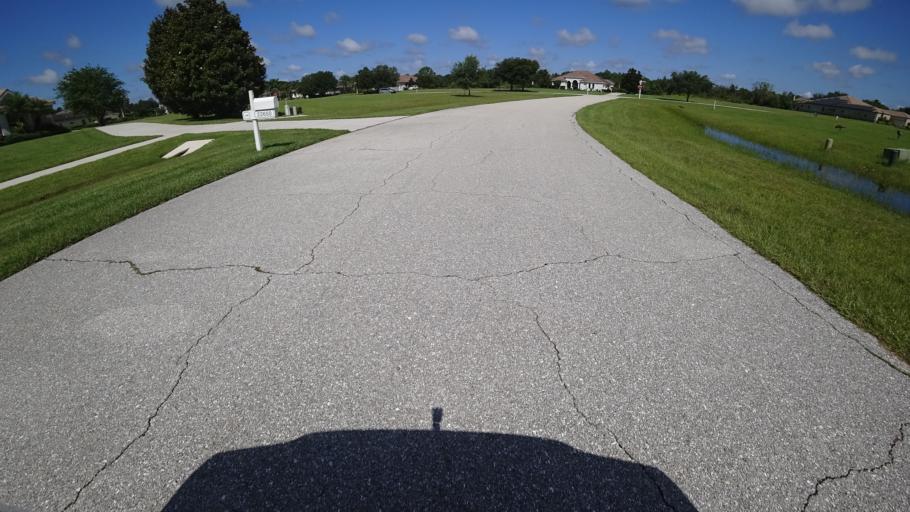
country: US
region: Florida
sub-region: Sarasota County
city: Fruitville
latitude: 27.3918
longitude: -82.3147
